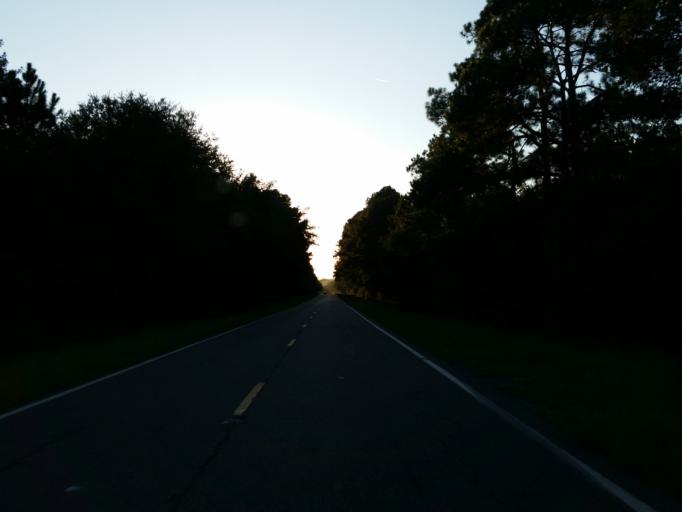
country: US
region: Georgia
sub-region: Berrien County
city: Ray City
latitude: 31.1752
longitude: -83.1196
